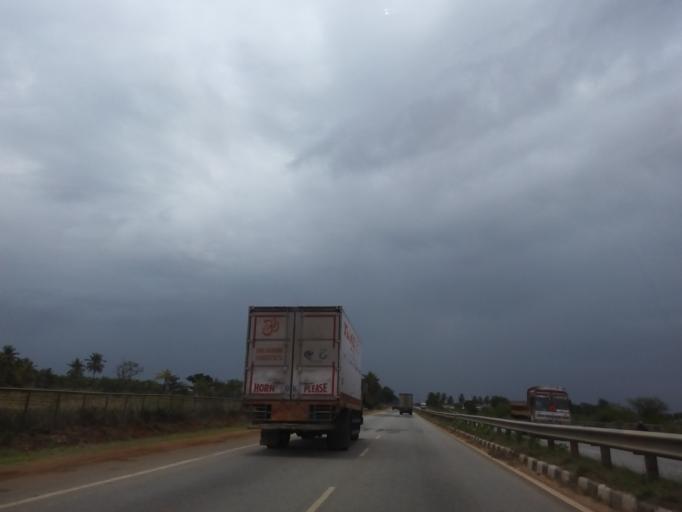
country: IN
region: Karnataka
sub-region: Davanagere
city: Harihar
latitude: 14.4650
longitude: 75.8456
